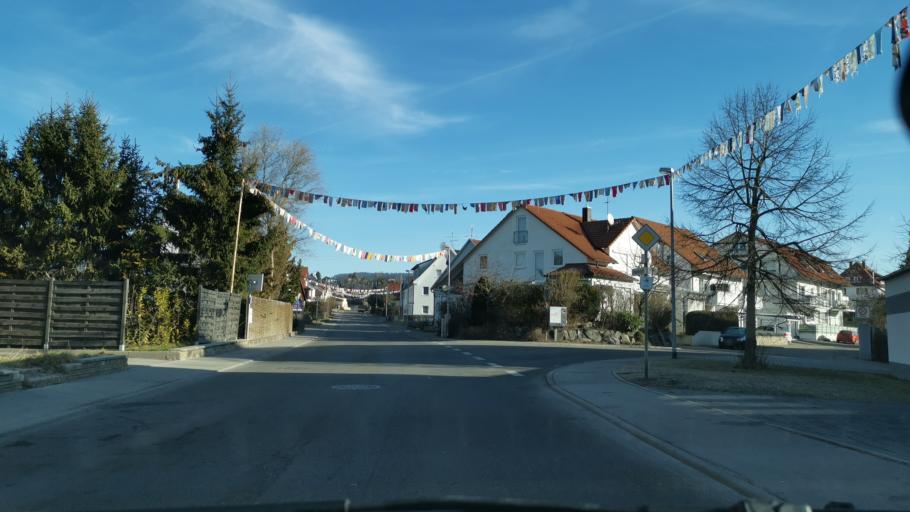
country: DE
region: Baden-Wuerttemberg
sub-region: Regierungsbezirk Stuttgart
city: Herrenberg
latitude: 48.5590
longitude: 8.9070
